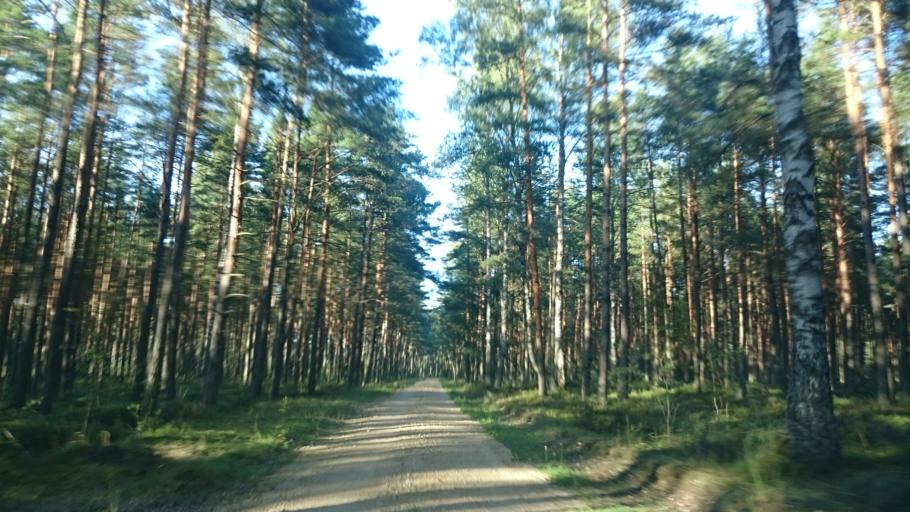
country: LV
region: Carnikava
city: Carnikava
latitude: 57.1101
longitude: 24.2396
